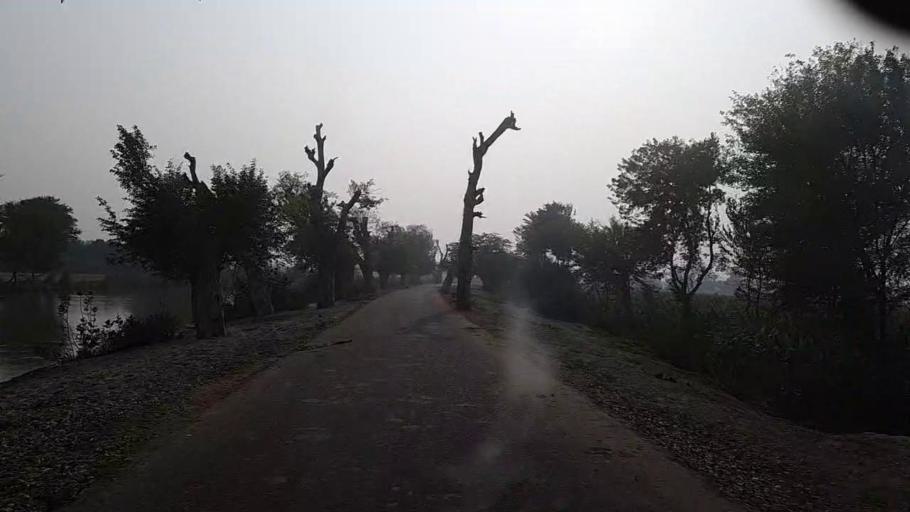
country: PK
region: Sindh
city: Bozdar
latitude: 27.1458
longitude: 68.6590
